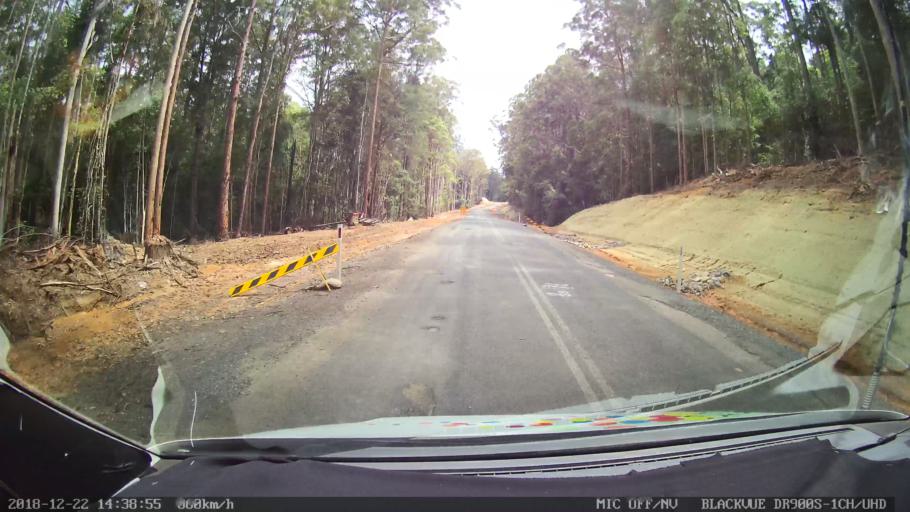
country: AU
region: New South Wales
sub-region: Bellingen
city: Dorrigo
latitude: -30.1421
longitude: 152.5949
